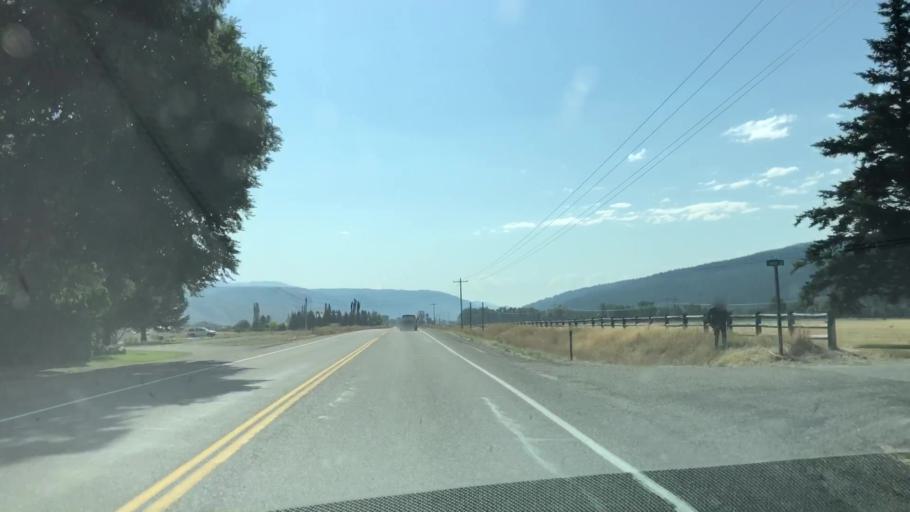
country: US
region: Idaho
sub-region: Teton County
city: Victor
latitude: 43.4005
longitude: -111.2865
